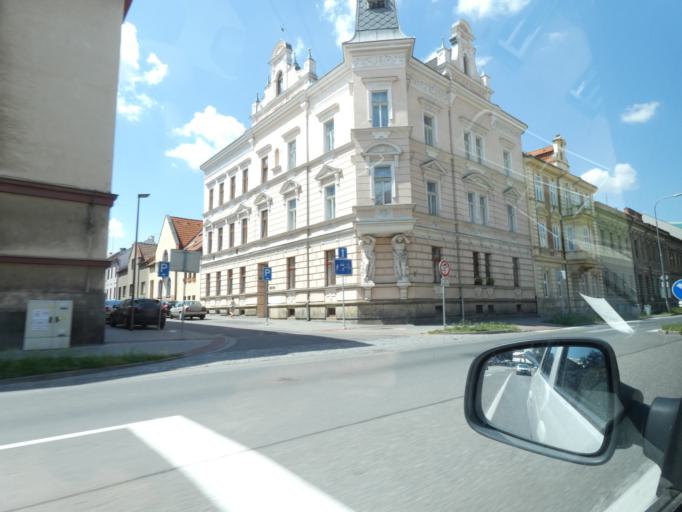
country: CZ
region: Pardubicky
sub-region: Okres Chrudim
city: Chrudim
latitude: 49.9506
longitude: 15.7886
